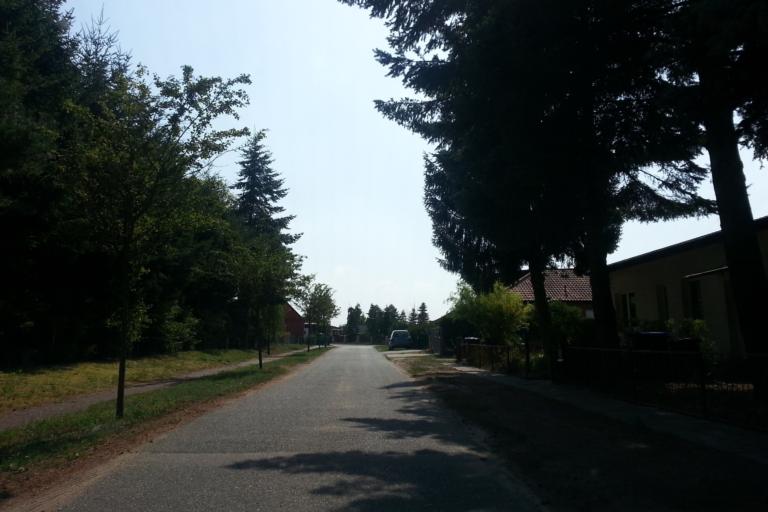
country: DE
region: Mecklenburg-Vorpommern
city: Ferdinandshof
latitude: 53.5942
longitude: 13.8261
